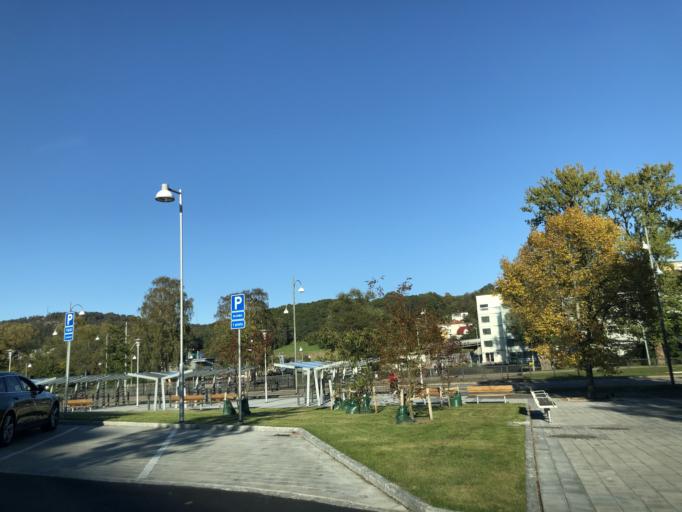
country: SE
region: Vaestra Goetaland
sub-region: Molndal
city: Moelndal
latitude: 57.6612
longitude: 12.0129
